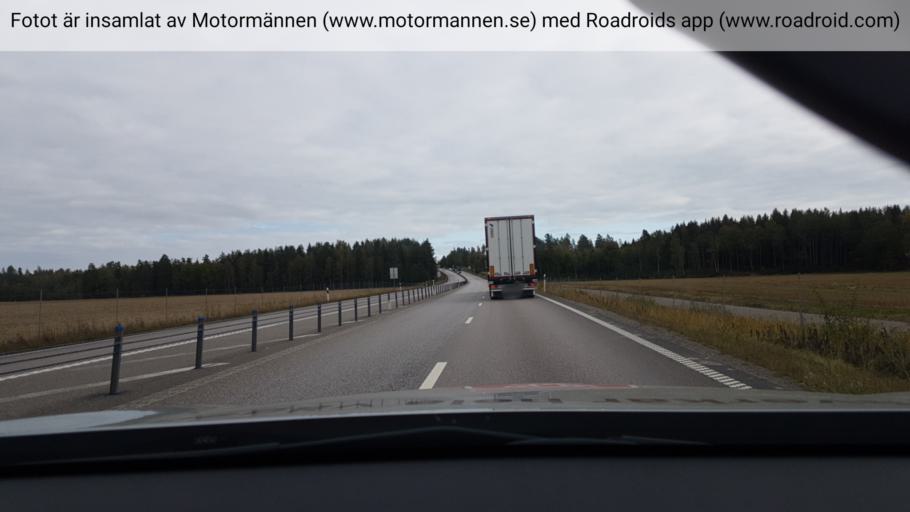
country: SE
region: Vaestra Goetaland
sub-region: Toreboda Kommun
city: Toereboda
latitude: 58.8054
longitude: 14.0995
